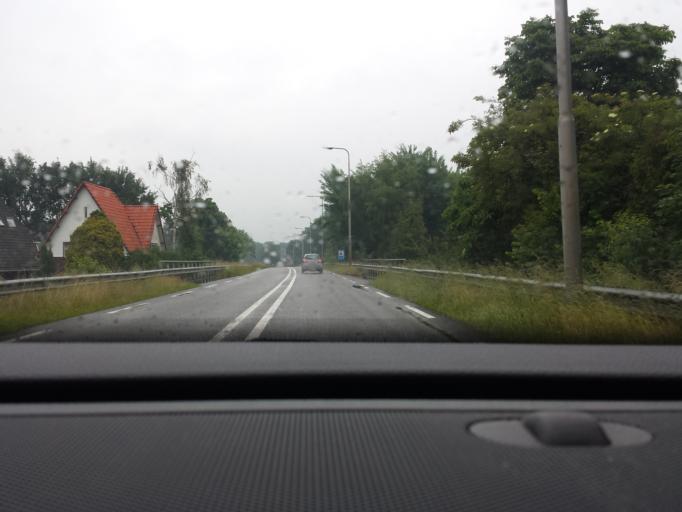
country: NL
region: Overijssel
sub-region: Gemeente Haaksbergen
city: Haaksbergen
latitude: 52.1539
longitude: 6.7499
